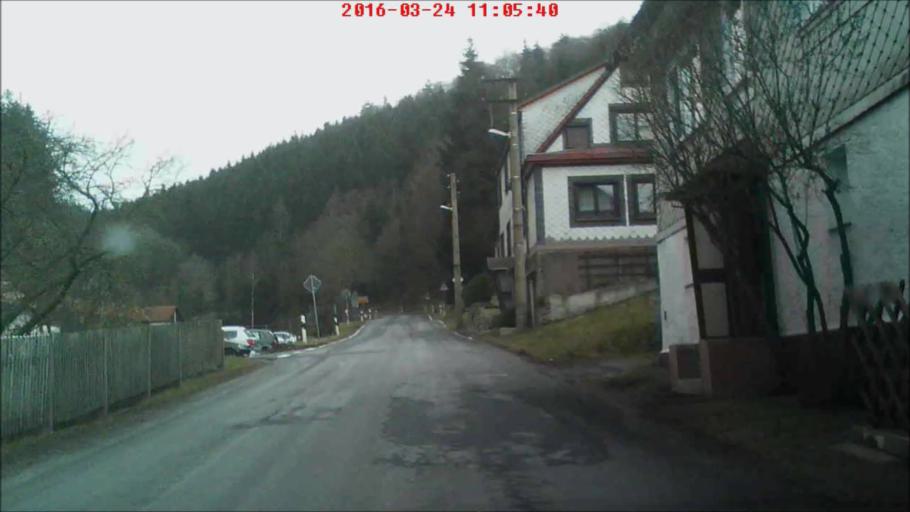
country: DE
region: Thuringia
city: Neustadt am Rennsteig
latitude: 50.5360
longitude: 10.9218
